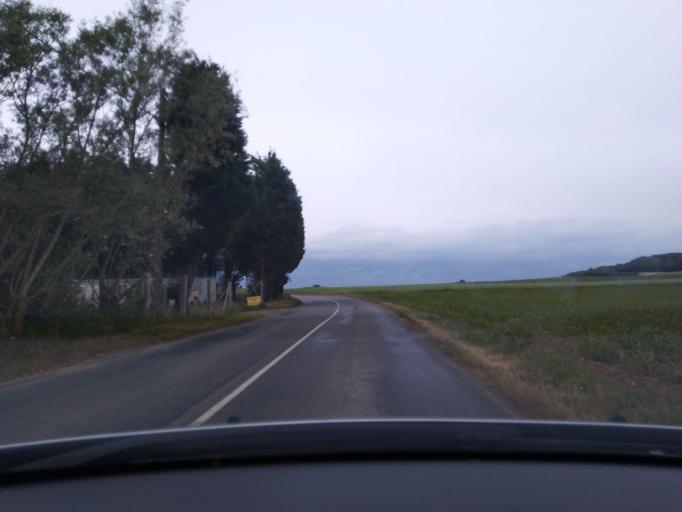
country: FR
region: Nord-Pas-de-Calais
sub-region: Departement du Pas-de-Calais
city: Wissant
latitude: 50.8619
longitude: 1.6734
